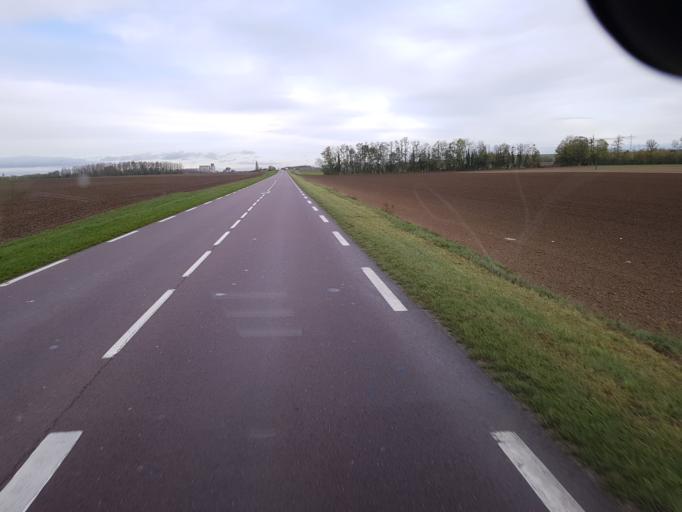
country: FR
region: Champagne-Ardenne
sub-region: Departement de l'Aube
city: Lusigny-sur-Barse
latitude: 48.2733
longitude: 4.2040
